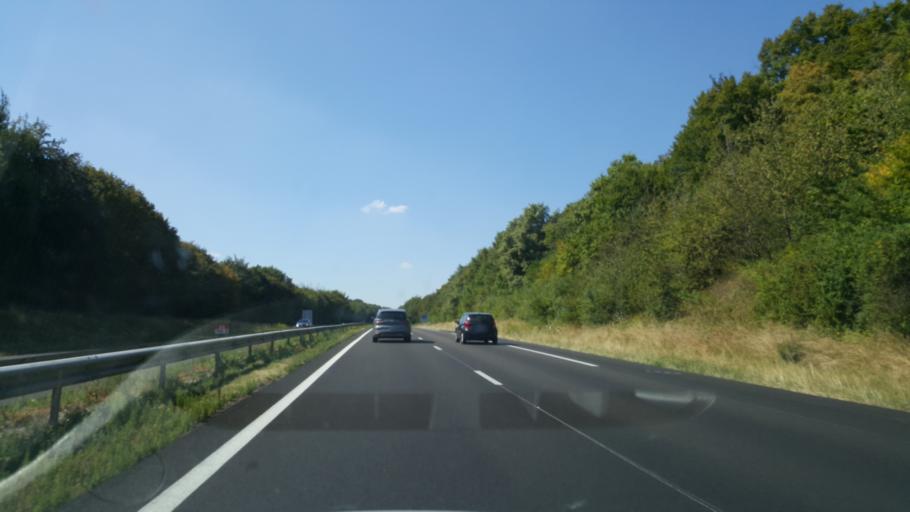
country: FR
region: Bourgogne
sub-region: Departement de l'Yonne
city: Joux-la-Ville
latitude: 47.5834
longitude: 3.9260
